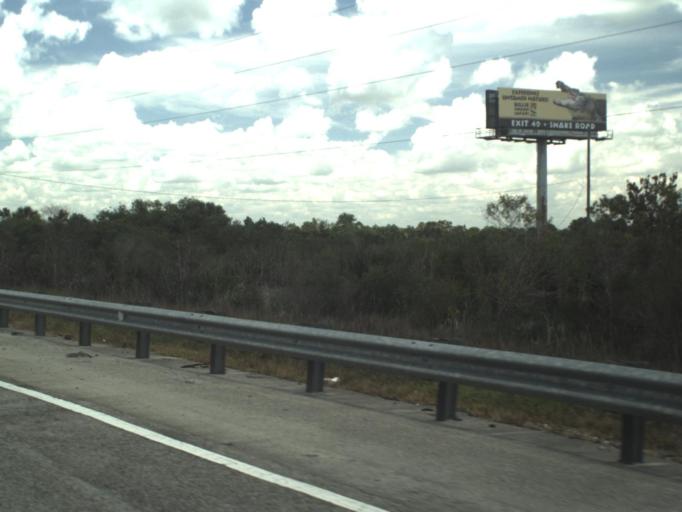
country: US
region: Florida
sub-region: Broward County
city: Weston
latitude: 26.1674
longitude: -80.8337
